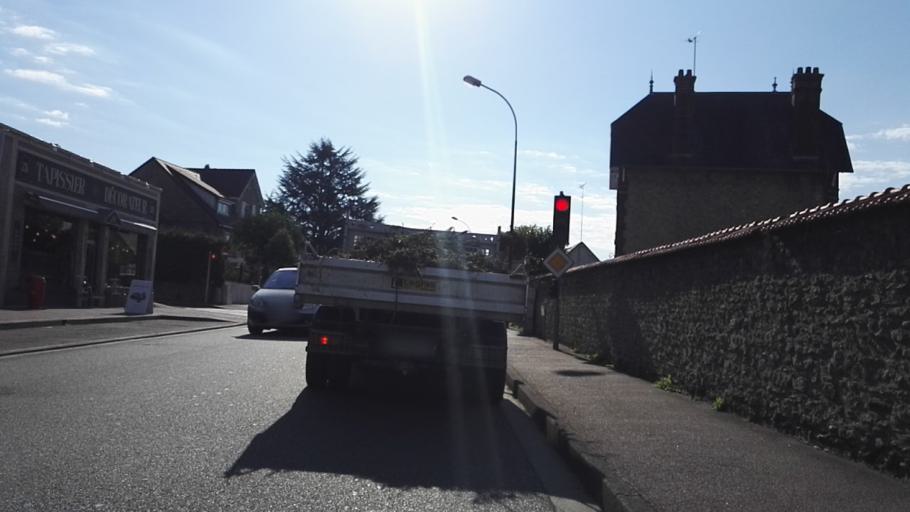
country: FR
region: Haute-Normandie
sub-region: Departement de l'Eure
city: Pacy-sur-Eure
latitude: 49.0188
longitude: 1.3809
